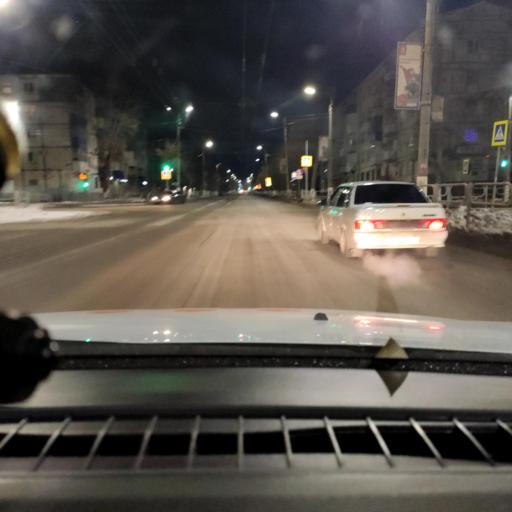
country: RU
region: Samara
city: Novokuybyshevsk
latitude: 53.0911
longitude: 49.9500
